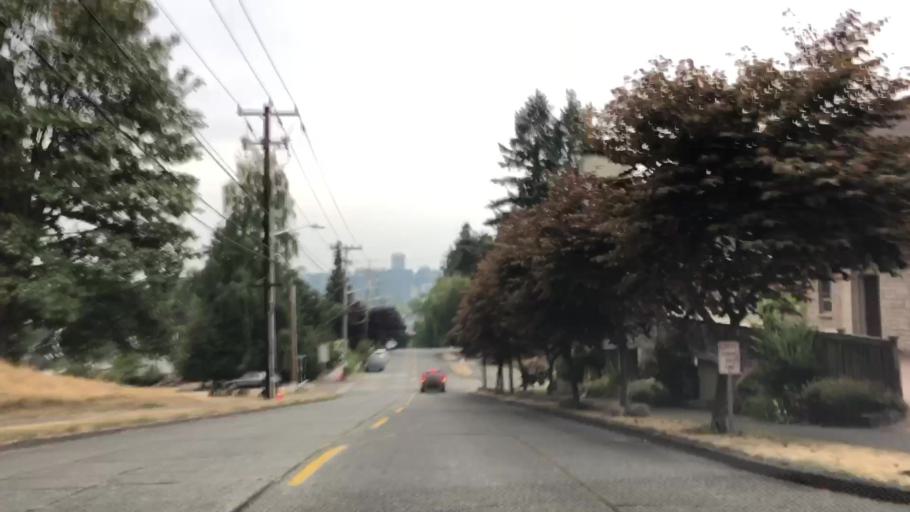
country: US
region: Washington
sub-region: King County
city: Yarrow Point
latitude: 47.6613
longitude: -122.2783
